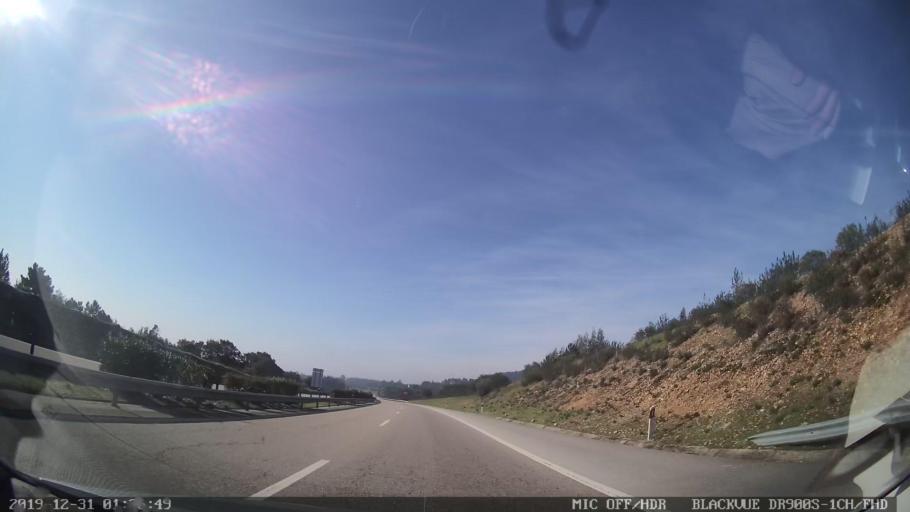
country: PT
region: Santarem
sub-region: Constancia
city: Constancia
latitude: 39.4928
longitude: -8.3019
